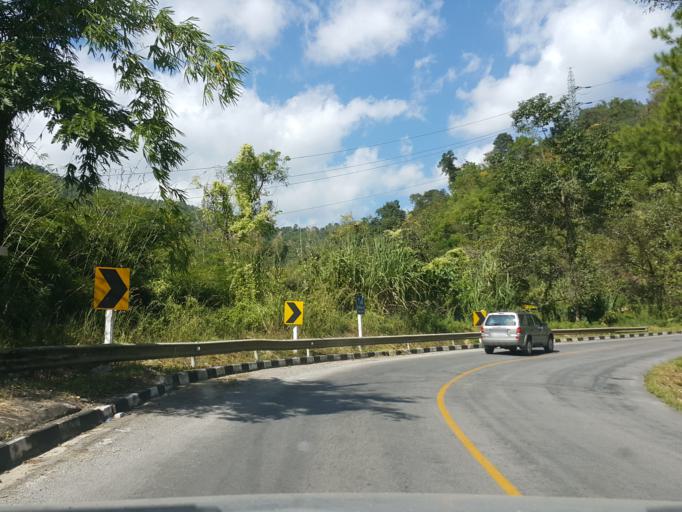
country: TH
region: Mae Hong Son
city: Mae Hi
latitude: 19.2213
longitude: 98.6717
